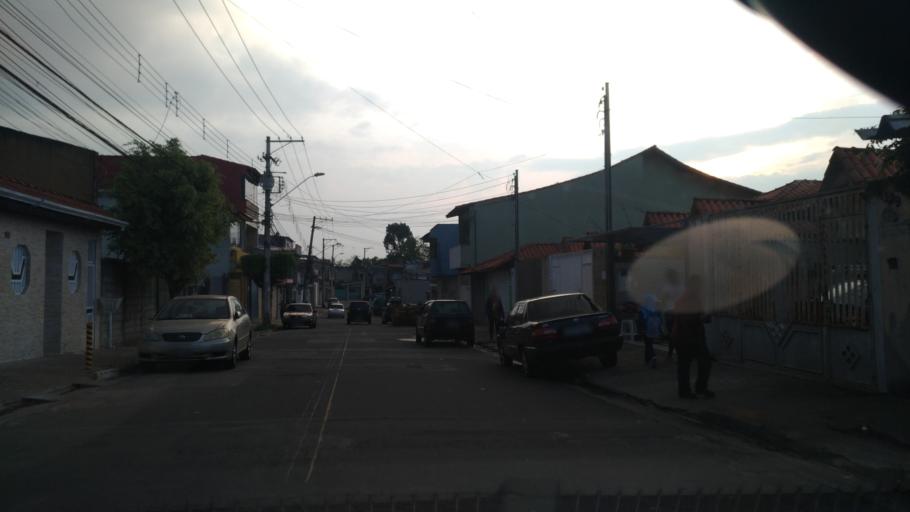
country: BR
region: Sao Paulo
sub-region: Itaquaquecetuba
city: Itaquaquecetuba
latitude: -23.4326
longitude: -46.4293
